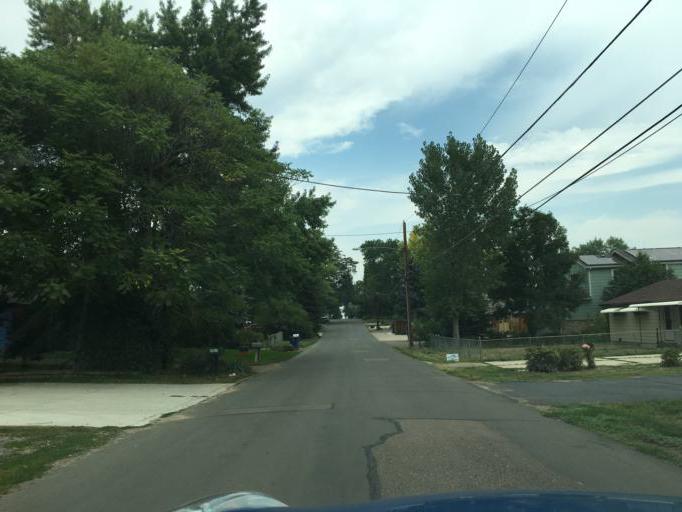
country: US
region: Colorado
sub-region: Jefferson County
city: Wheat Ridge
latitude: 39.7486
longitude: -105.1020
